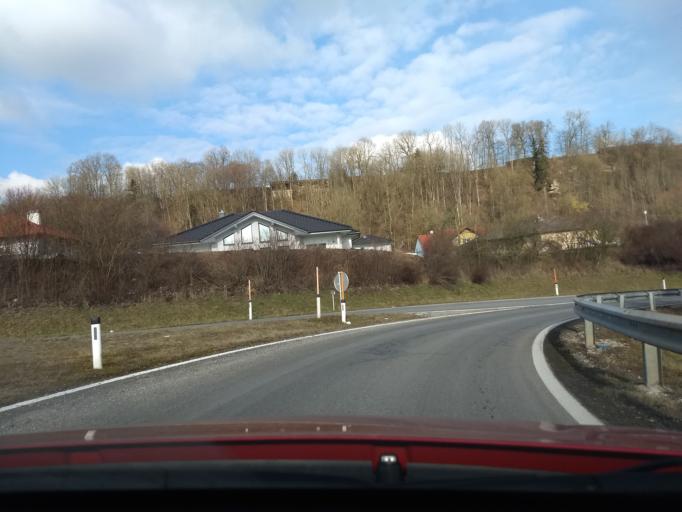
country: AT
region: Upper Austria
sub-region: Politischer Bezirk Steyr-Land
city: Sierning
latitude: 48.0555
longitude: 14.3427
